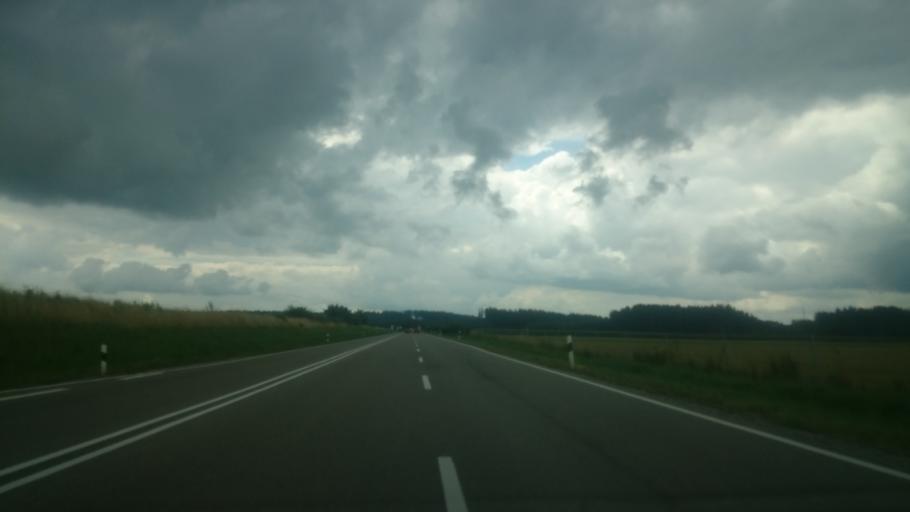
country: DE
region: Bavaria
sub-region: Swabia
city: Rieden
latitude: 47.9213
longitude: 10.6589
